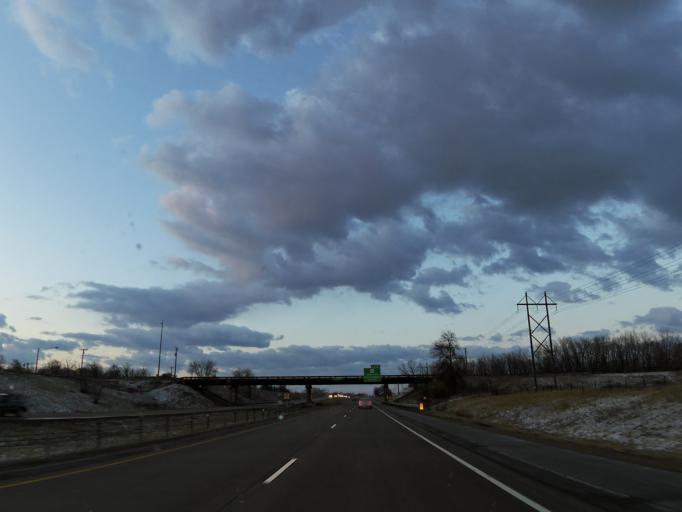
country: US
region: Minnesota
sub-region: Dakota County
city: Lakeville
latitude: 44.6682
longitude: -93.2943
